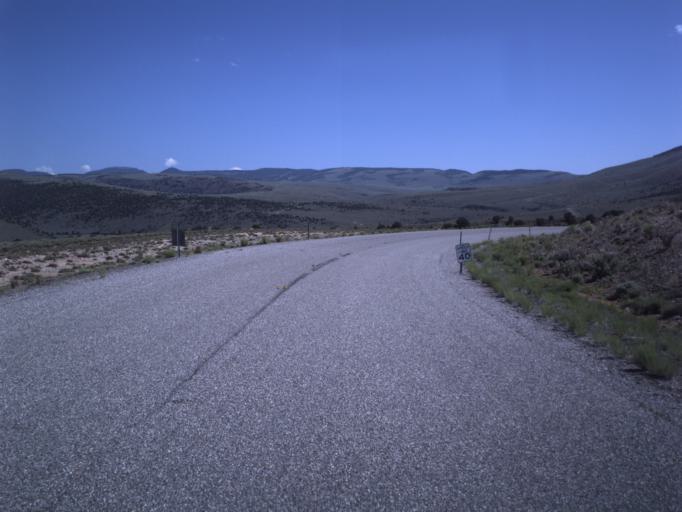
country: US
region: Utah
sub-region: Wayne County
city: Loa
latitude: 38.5063
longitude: -111.5299
